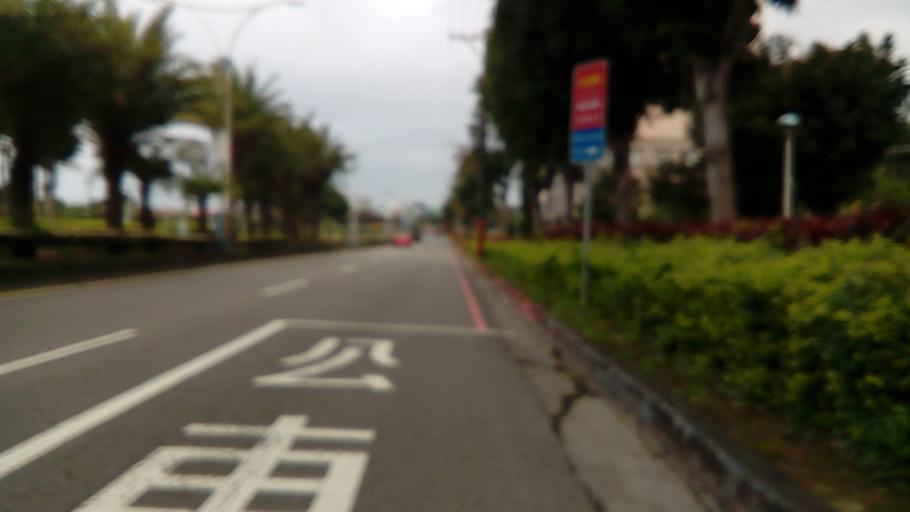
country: TW
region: Taipei
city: Taipei
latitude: 25.1784
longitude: 121.4234
